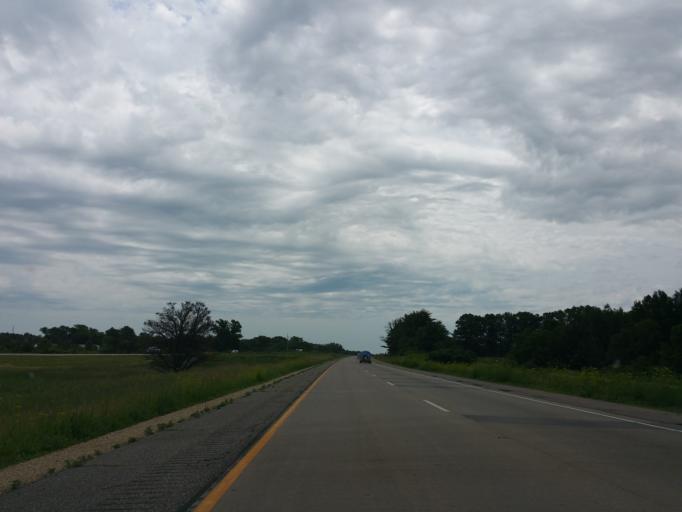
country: US
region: Wisconsin
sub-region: Juneau County
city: Mauston
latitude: 43.8431
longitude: -90.0976
